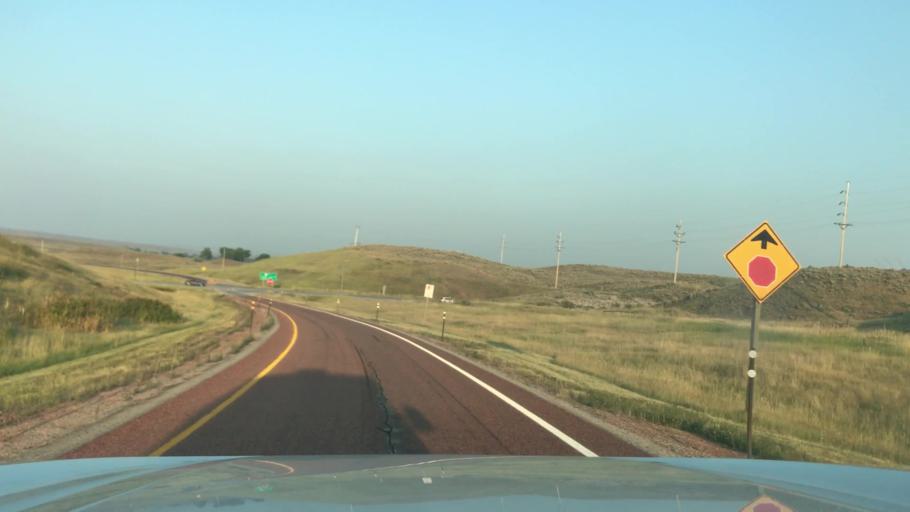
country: US
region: Wyoming
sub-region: Sheridan County
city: Sheridan
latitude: 44.9147
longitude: -107.1542
